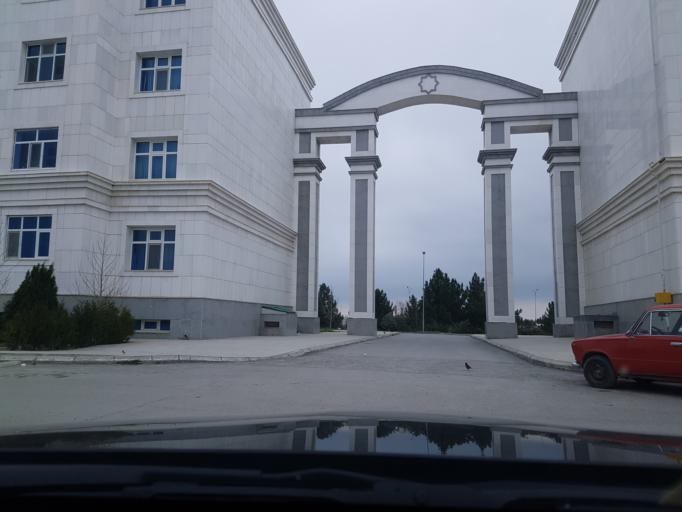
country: TM
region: Ahal
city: Abadan
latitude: 38.1632
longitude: 57.9394
